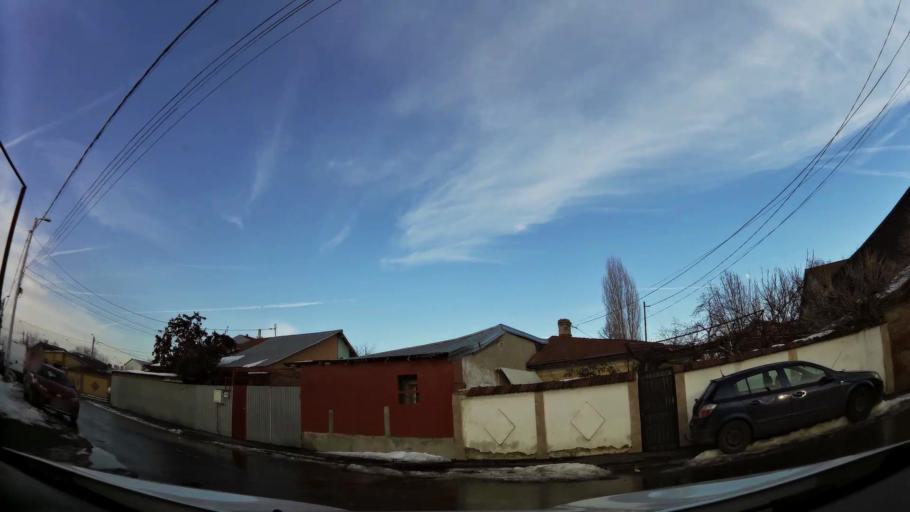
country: RO
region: Bucuresti
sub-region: Municipiul Bucuresti
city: Bucuresti
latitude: 44.3924
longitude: 26.0835
